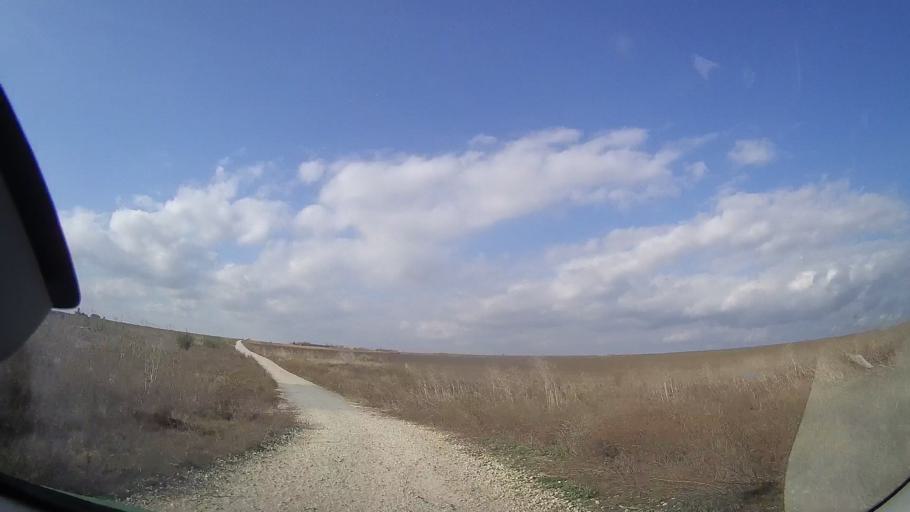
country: RO
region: Constanta
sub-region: Comuna Douazeci si Trei August
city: Douazeci si Trei August
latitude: 43.9094
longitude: 28.6077
